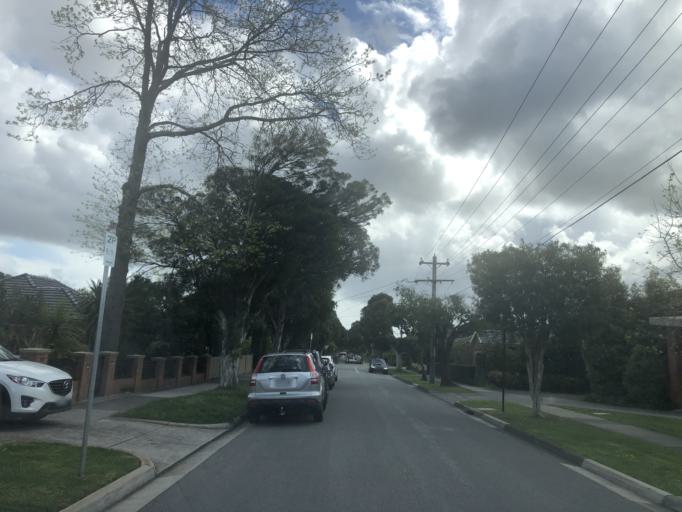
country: AU
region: Victoria
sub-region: Monash
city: Ashwood
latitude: -37.8780
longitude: 145.1259
